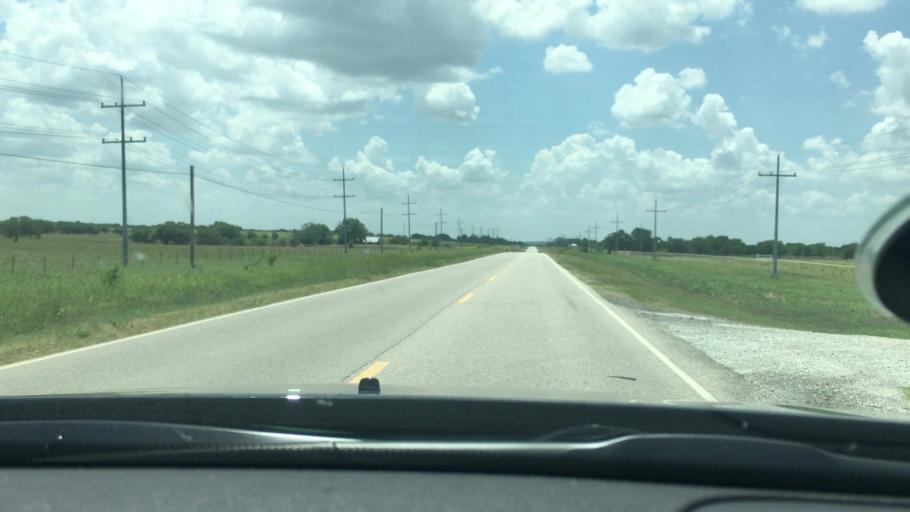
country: US
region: Oklahoma
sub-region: Pontotoc County
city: Ada
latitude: 34.6429
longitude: -96.6348
